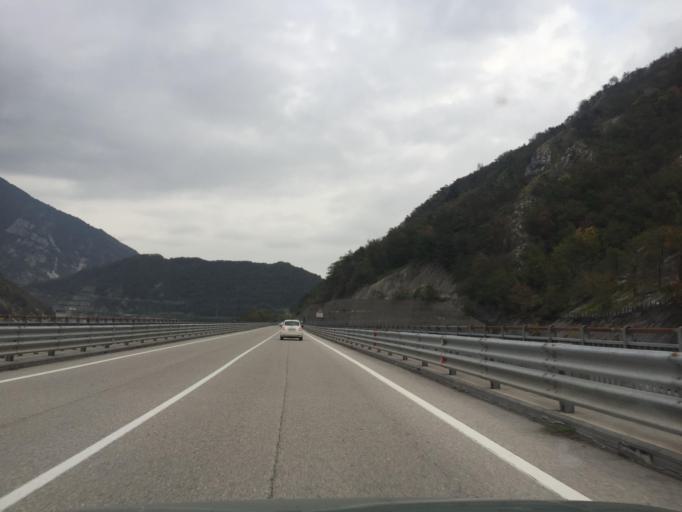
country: IT
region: Friuli Venezia Giulia
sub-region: Provincia di Pordenone
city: Montereale Valcellina
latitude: 46.1649
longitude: 12.6374
